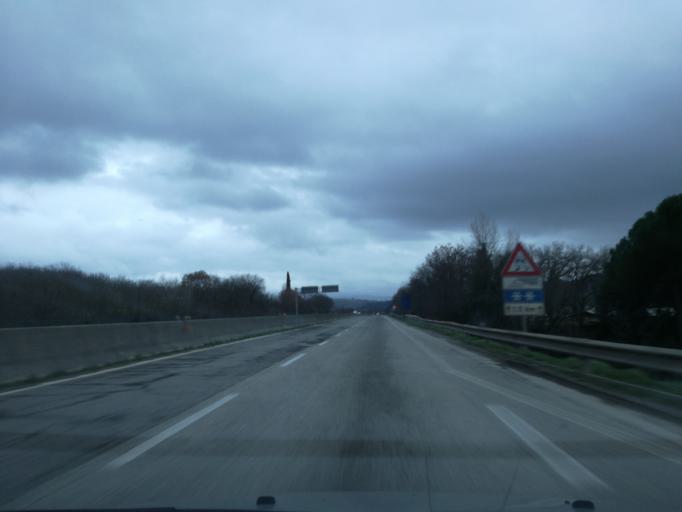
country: IT
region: Umbria
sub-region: Provincia di Perugia
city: Ponte Felcino
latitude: 43.1231
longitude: 12.4515
